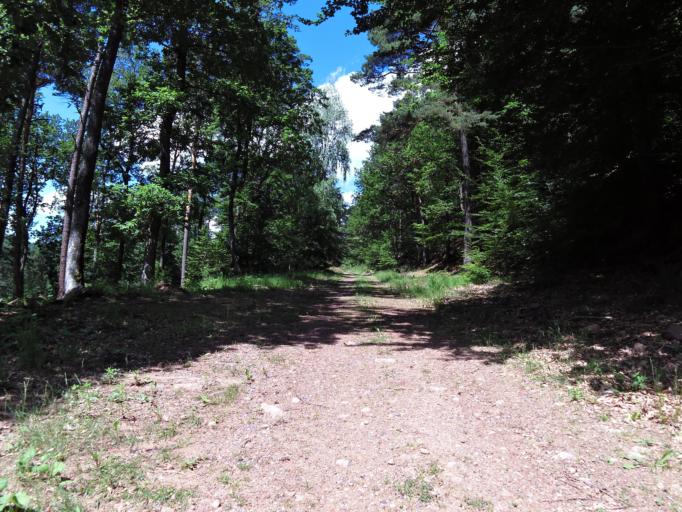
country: DE
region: Rheinland-Pfalz
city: Ramberg
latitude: 49.2967
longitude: 8.0488
